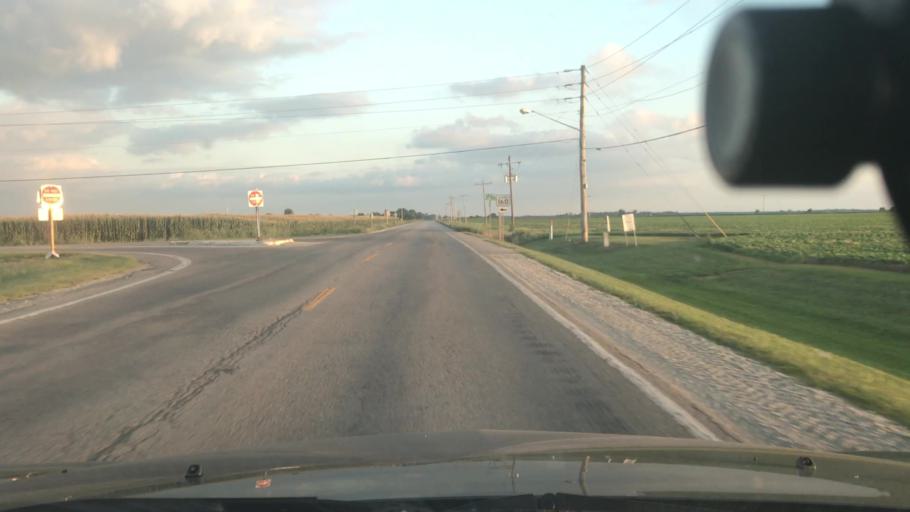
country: US
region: Illinois
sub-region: Washington County
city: Okawville
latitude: 38.4190
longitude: -89.5506
